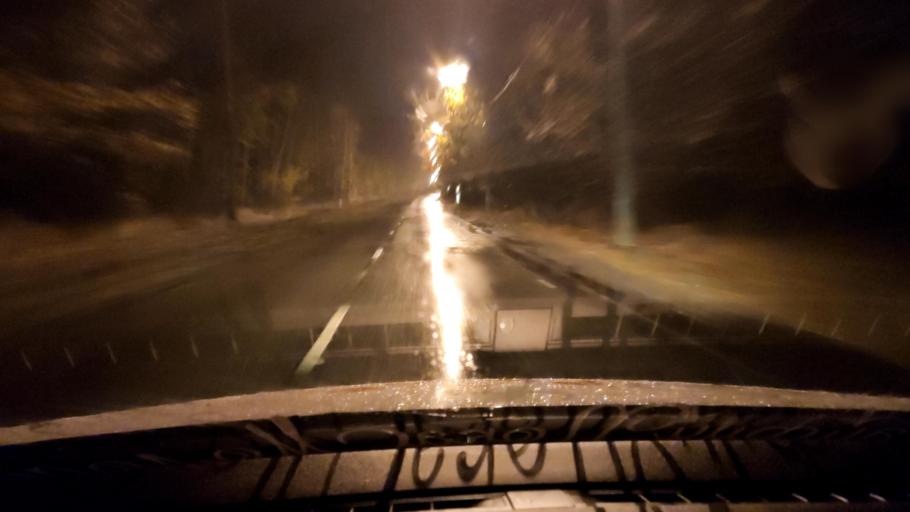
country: RU
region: Voronezj
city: Somovo
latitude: 51.7158
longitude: 39.3243
